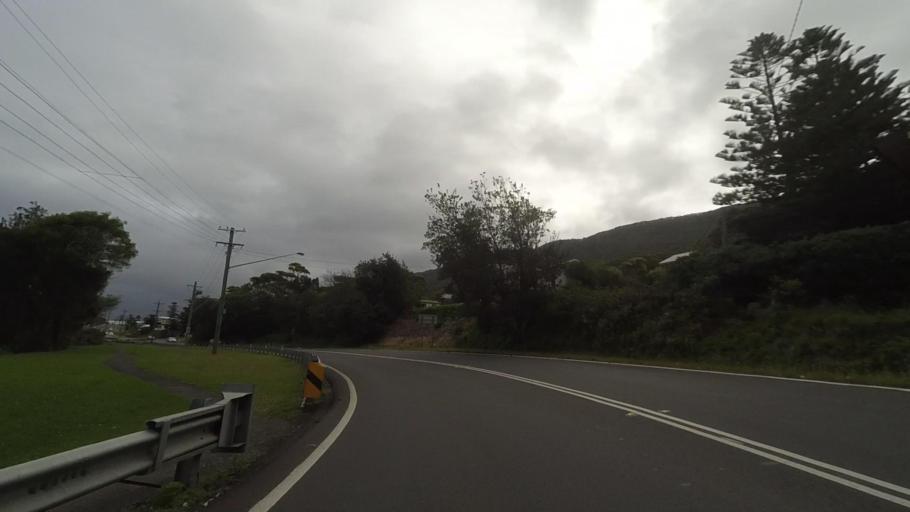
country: AU
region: New South Wales
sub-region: Wollongong
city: Bulli
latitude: -34.2857
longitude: 150.9492
